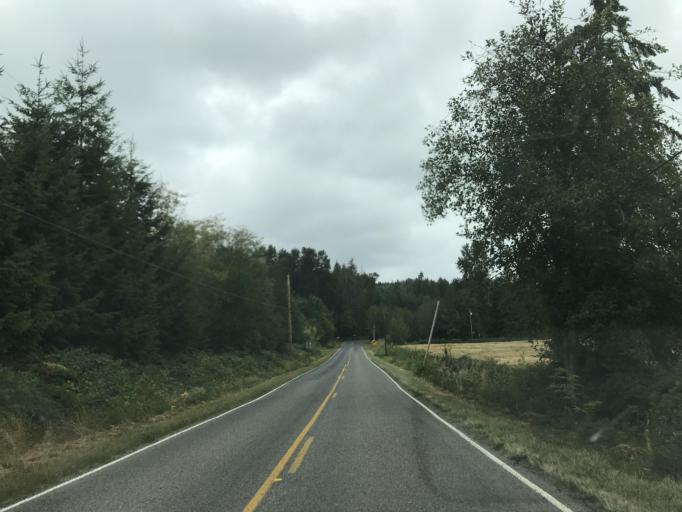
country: US
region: Washington
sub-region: Whatcom County
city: Sudden Valley
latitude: 48.7766
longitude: -122.3332
